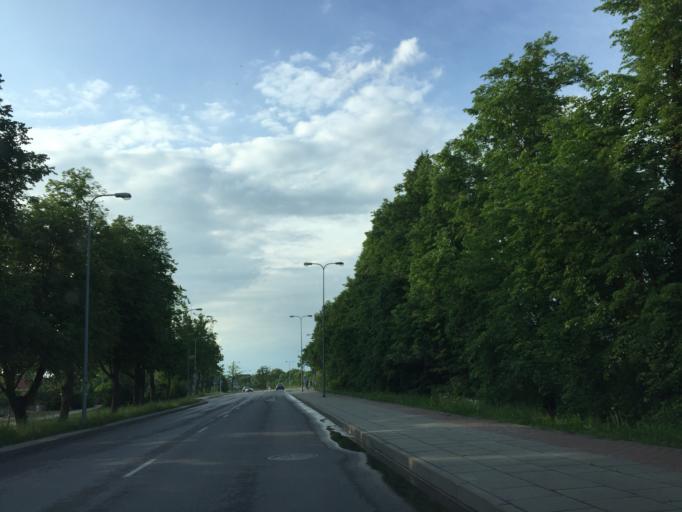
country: LT
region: Klaipedos apskritis
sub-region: Klaipeda
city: Klaipeda
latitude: 55.7516
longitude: 21.1334
